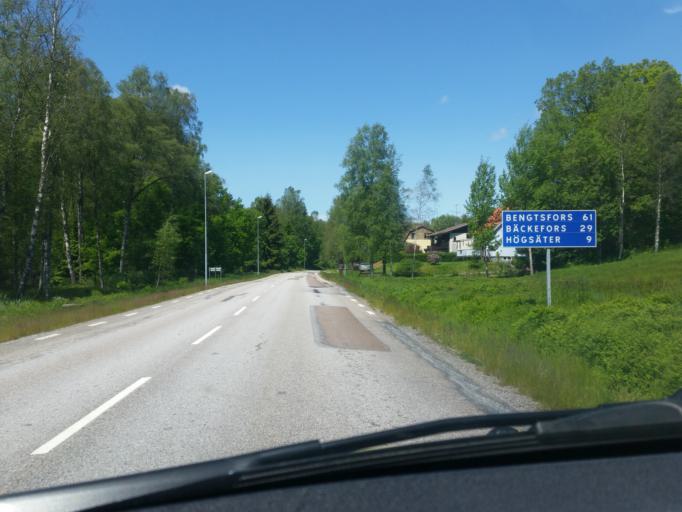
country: SE
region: Vaestra Goetaland
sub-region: Fargelanda Kommun
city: Faergelanda
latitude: 58.5697
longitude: 12.0575
